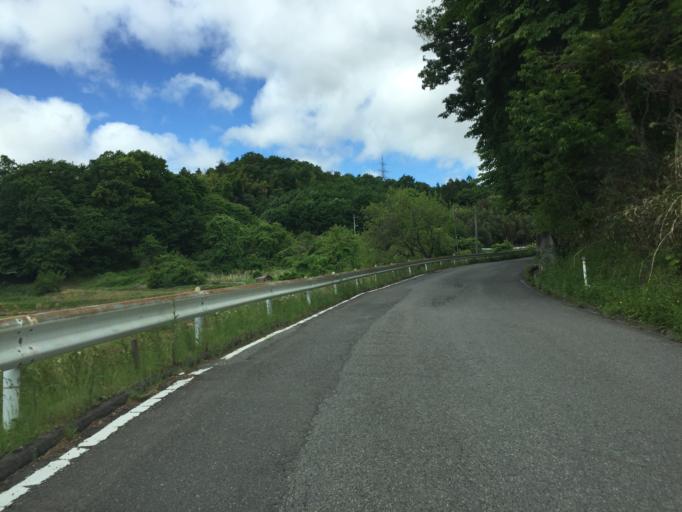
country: JP
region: Fukushima
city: Miharu
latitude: 37.4641
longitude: 140.4676
